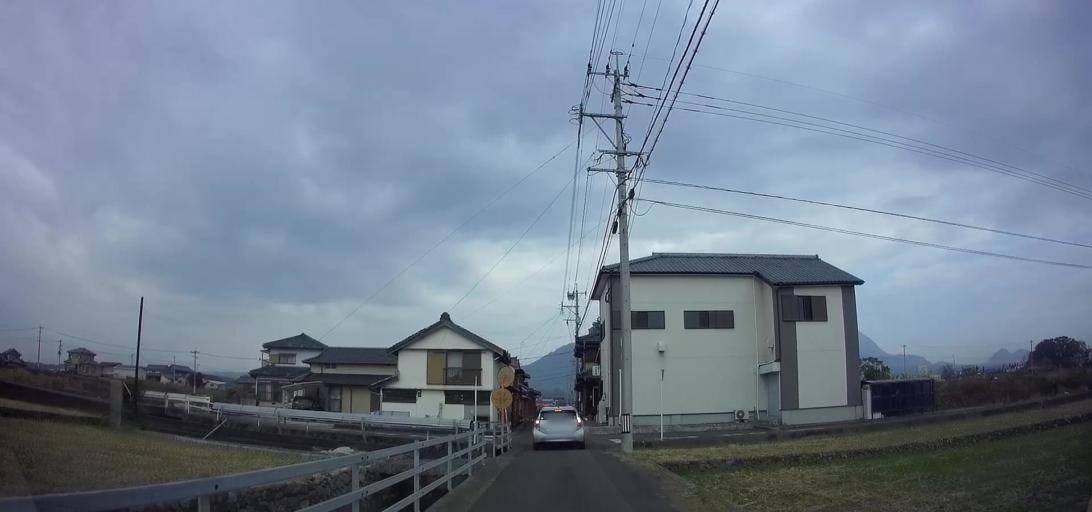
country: JP
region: Nagasaki
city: Shimabara
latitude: 32.6572
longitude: 130.3079
